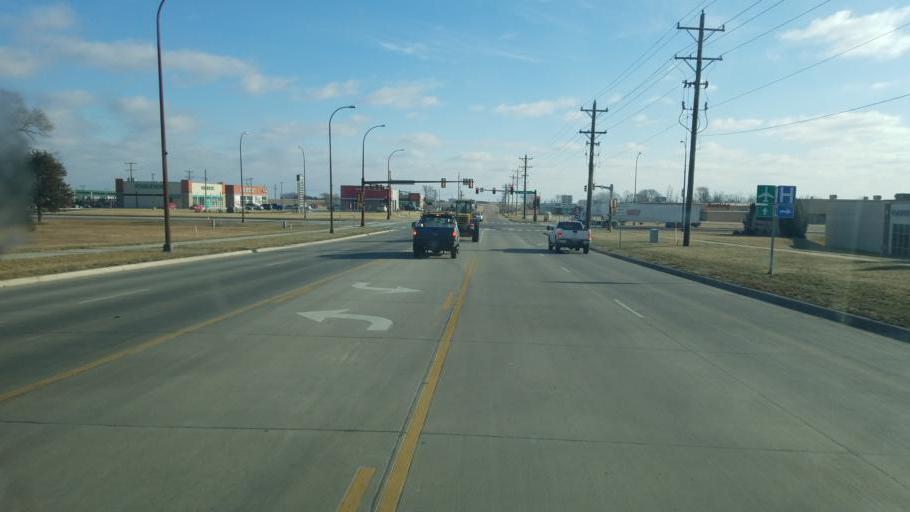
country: US
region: South Dakota
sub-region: Yankton County
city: Yankton
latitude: 42.9088
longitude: -97.3990
